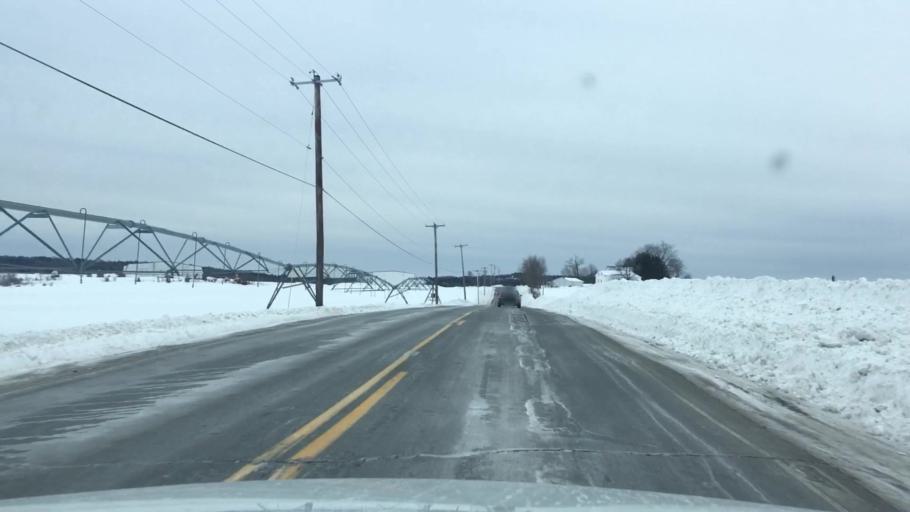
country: US
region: Maine
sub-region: Penobscot County
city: Garland
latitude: 44.9809
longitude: -69.0888
